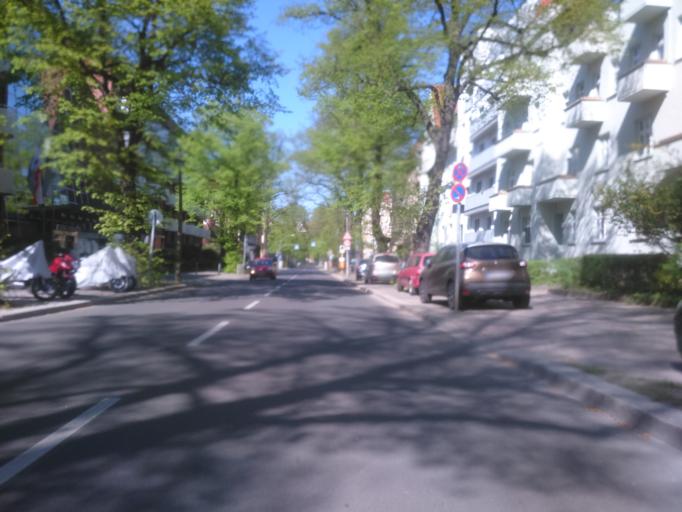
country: DE
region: Berlin
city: Weissensee
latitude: 52.5540
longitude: 13.4574
